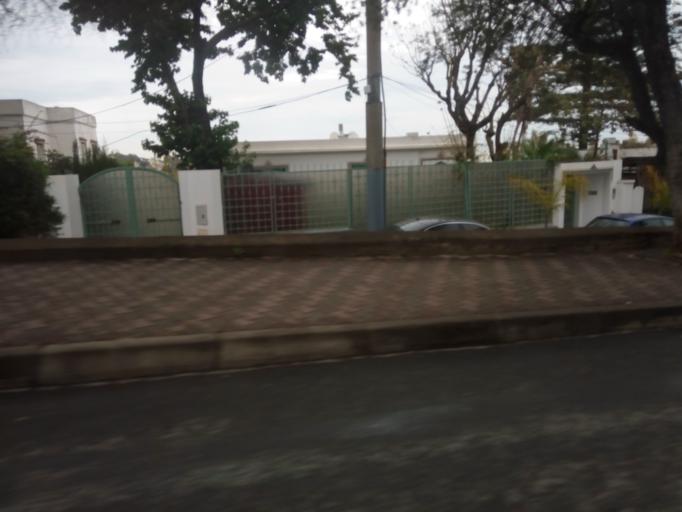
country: DZ
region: Alger
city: Algiers
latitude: 36.7531
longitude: 3.0274
